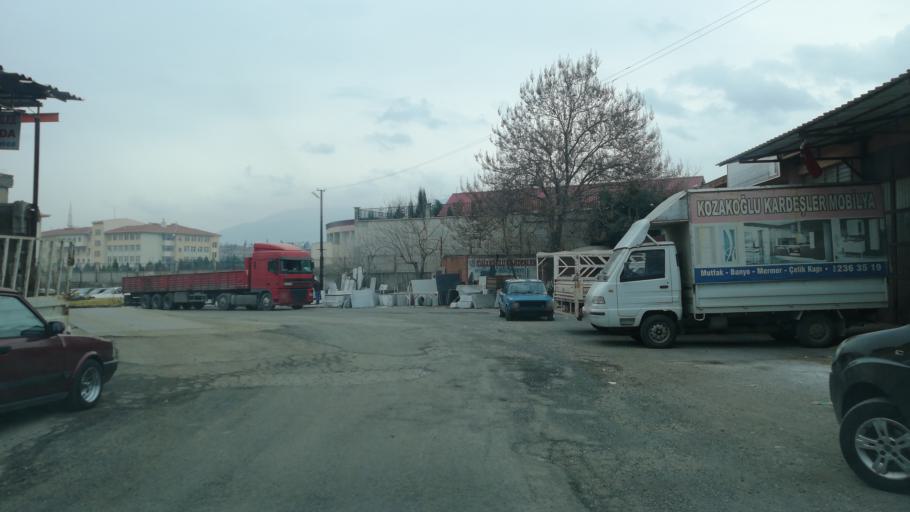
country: TR
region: Kahramanmaras
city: Kahramanmaras
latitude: 37.5675
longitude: 36.9590
